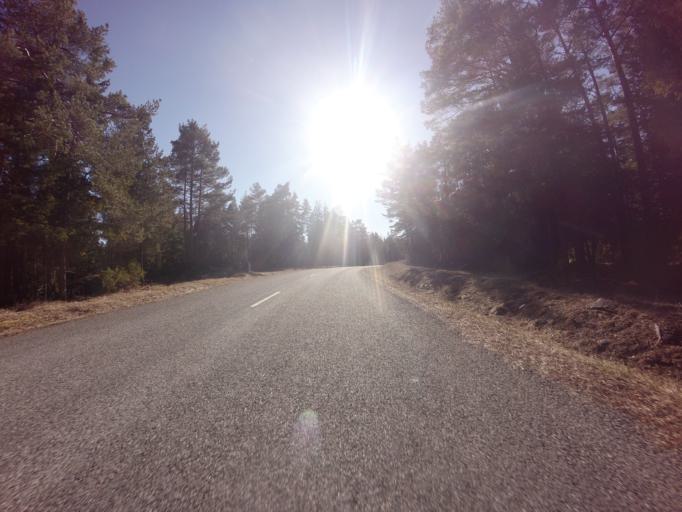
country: EE
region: Saare
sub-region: Kuressaare linn
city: Kuressaare
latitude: 58.5142
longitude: 22.3203
